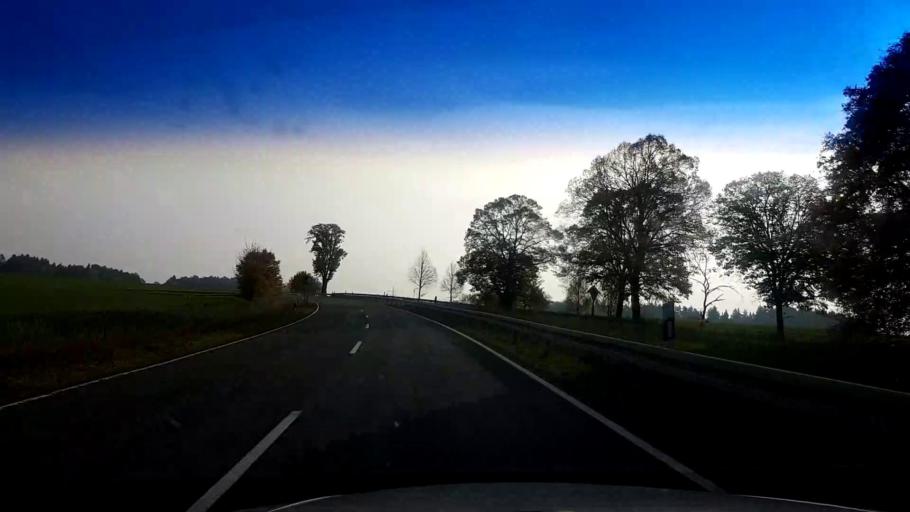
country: DE
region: Bavaria
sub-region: Upper Franconia
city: Stadelhofen
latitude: 50.0058
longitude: 11.1819
